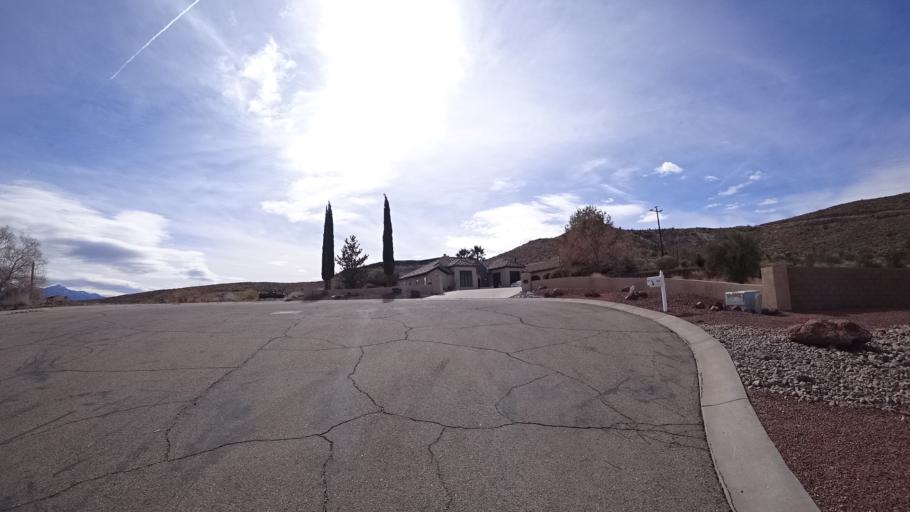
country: US
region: Arizona
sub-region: Mohave County
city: Kingman
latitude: 35.2302
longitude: -114.0577
